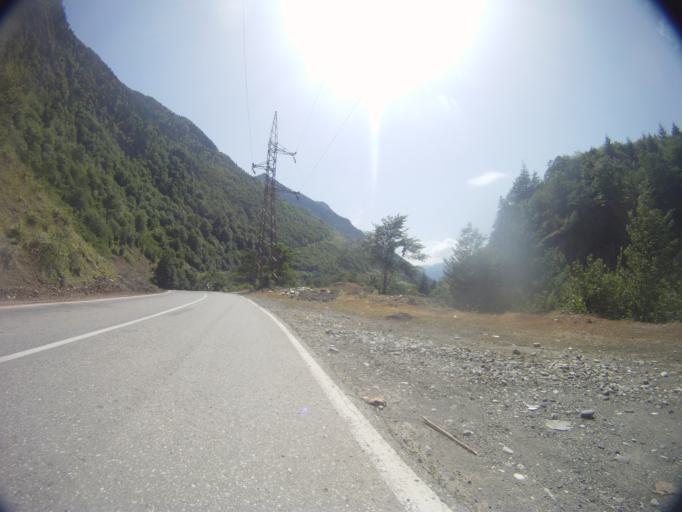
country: GE
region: Samegrelo and Zemo Svaneti
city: Jvari
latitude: 42.9442
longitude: 42.1753
